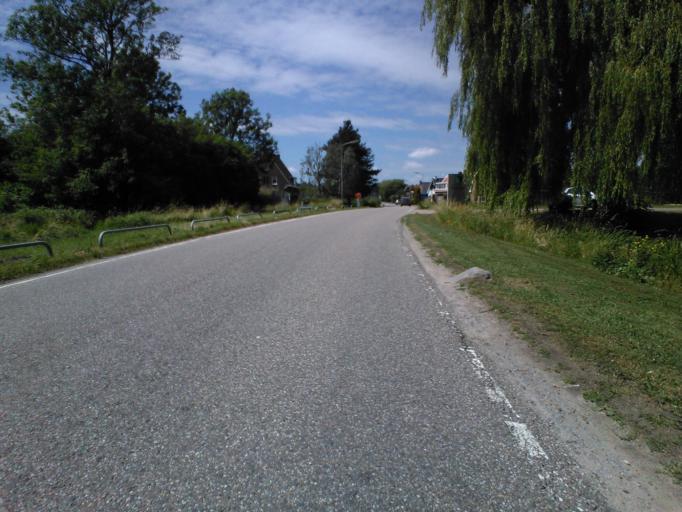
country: NL
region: South Holland
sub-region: Gemeente Alblasserdam
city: Alblasserdam
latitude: 51.8599
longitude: 4.6767
